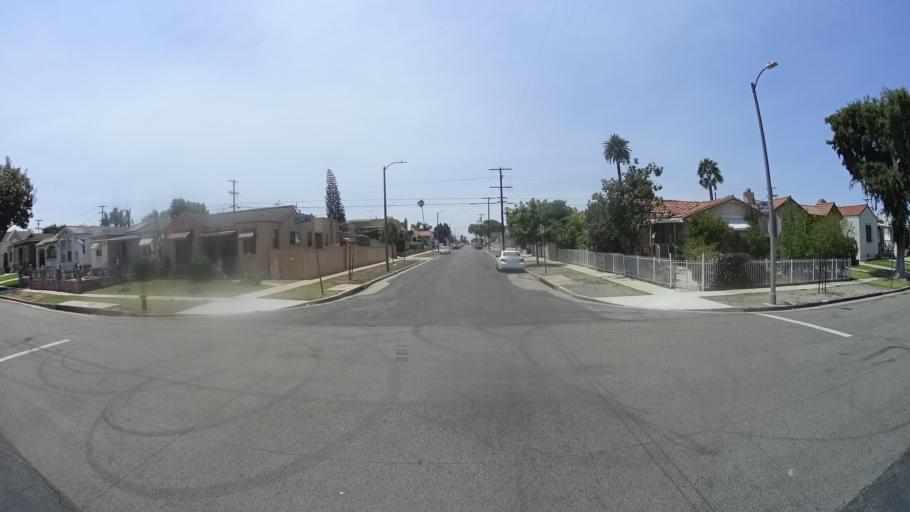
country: US
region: California
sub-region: Los Angeles County
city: Westmont
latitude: 33.9728
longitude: -118.3057
